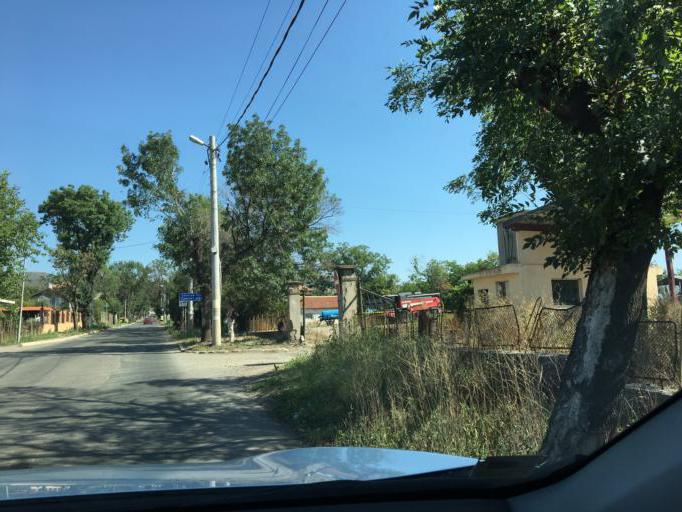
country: BG
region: Burgas
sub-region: Obshtina Kameno
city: Kameno
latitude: 42.6214
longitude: 27.3952
